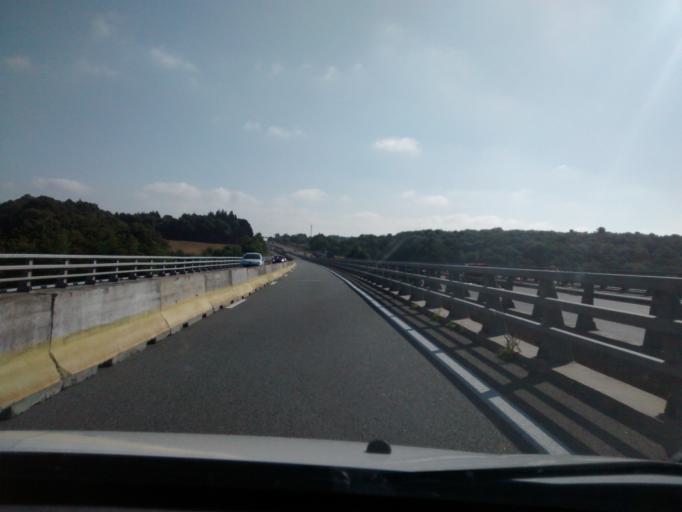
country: FR
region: Pays de la Loire
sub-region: Departement de la Mayenne
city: Saint-Berthevin
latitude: 48.0925
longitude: -0.8600
